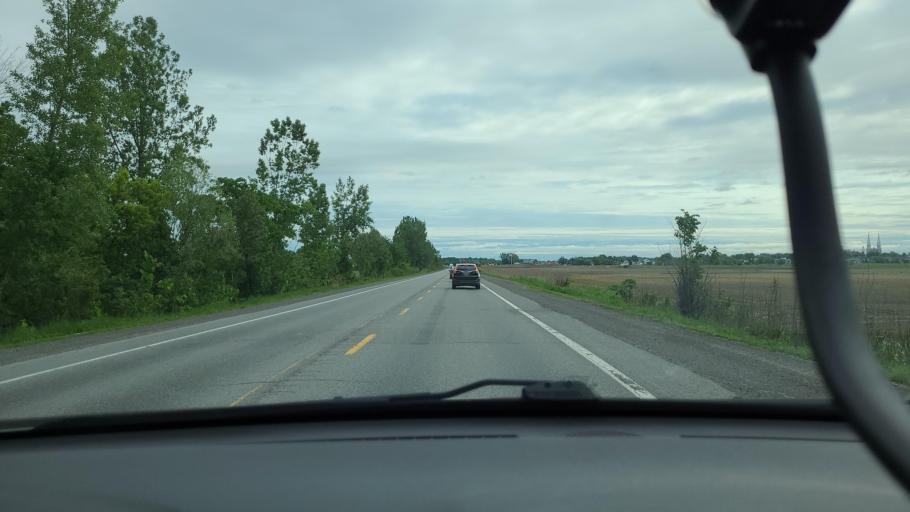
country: CA
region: Quebec
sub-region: Lanaudiere
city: Saint-Jacques
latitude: 45.9457
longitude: -73.5909
